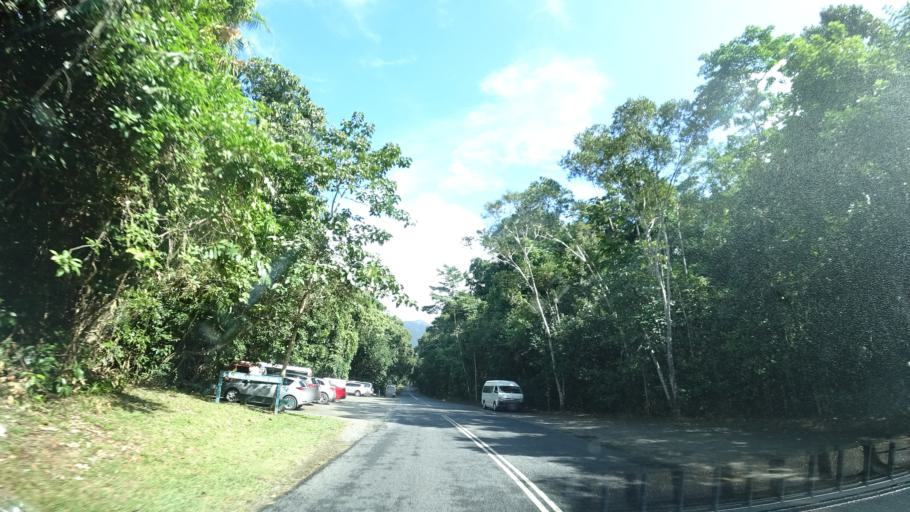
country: AU
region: Queensland
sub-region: Cairns
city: Port Douglas
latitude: -16.1379
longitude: 145.4411
